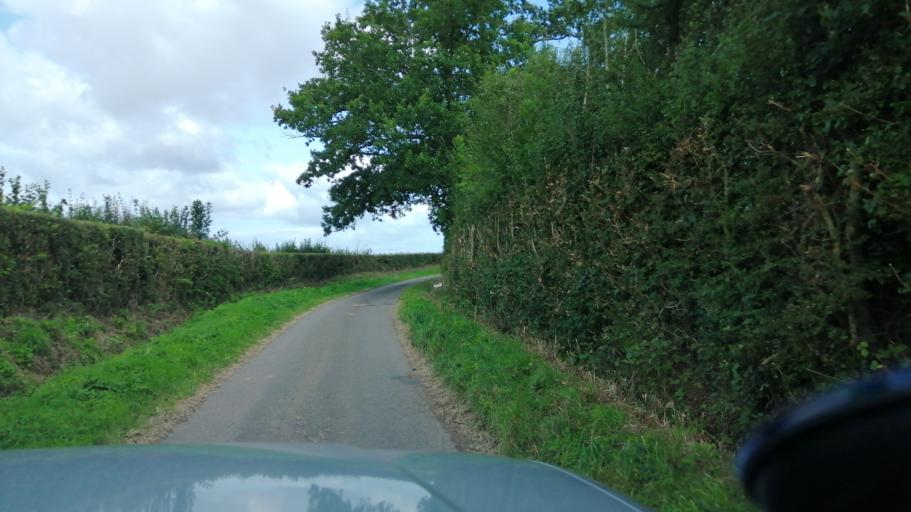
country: GB
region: England
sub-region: Herefordshire
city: Thruxton
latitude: 52.0224
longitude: -2.8047
